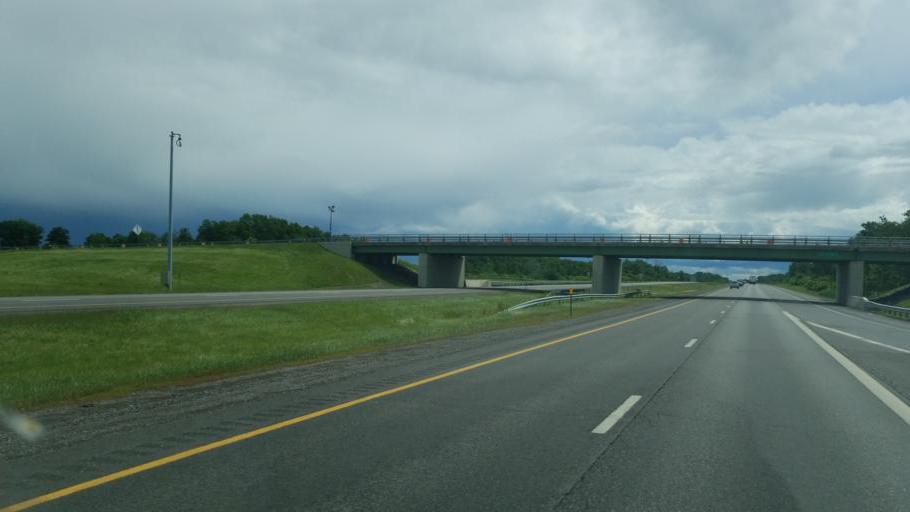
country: US
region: New York
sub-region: Genesee County
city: Le Roy
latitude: 43.0288
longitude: -77.9659
